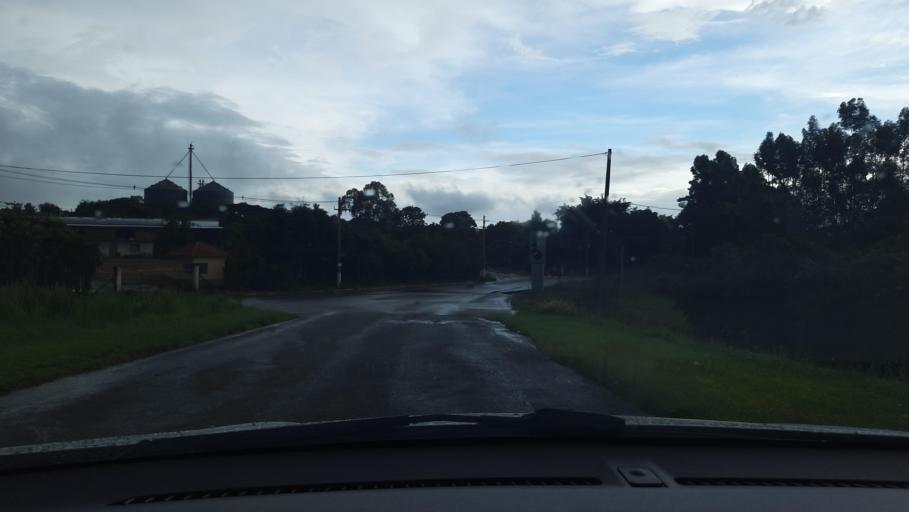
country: BR
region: Sao Paulo
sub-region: Casa Branca
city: Casa Branca
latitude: -21.7499
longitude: -47.0728
